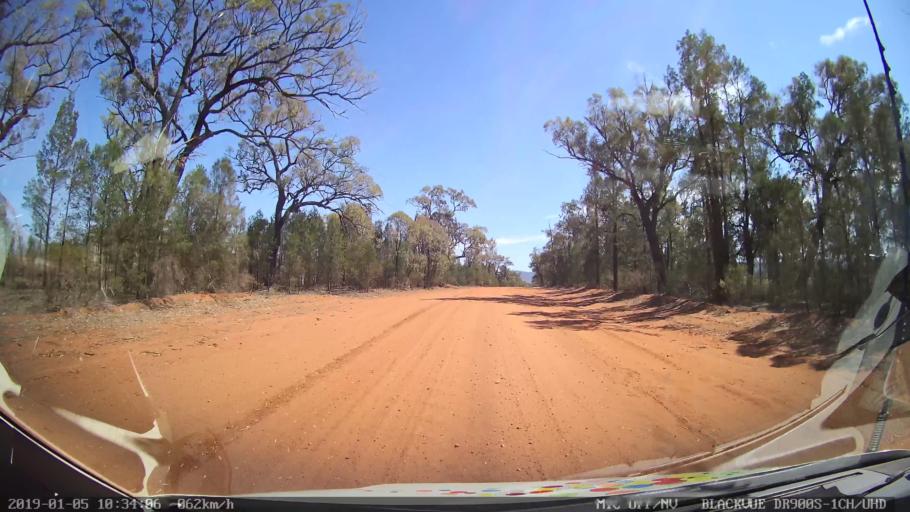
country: AU
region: New South Wales
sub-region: Gilgandra
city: Gilgandra
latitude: -31.5010
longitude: 148.9291
